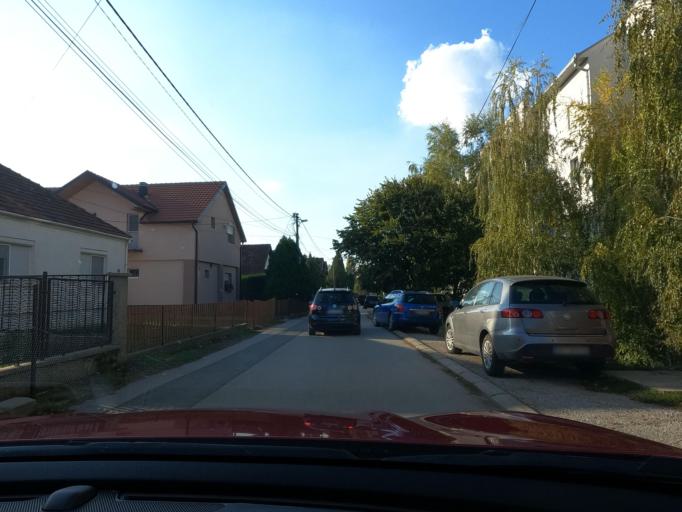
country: RS
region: Central Serbia
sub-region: Belgrade
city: Obrenovac
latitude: 44.6490
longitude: 20.1875
